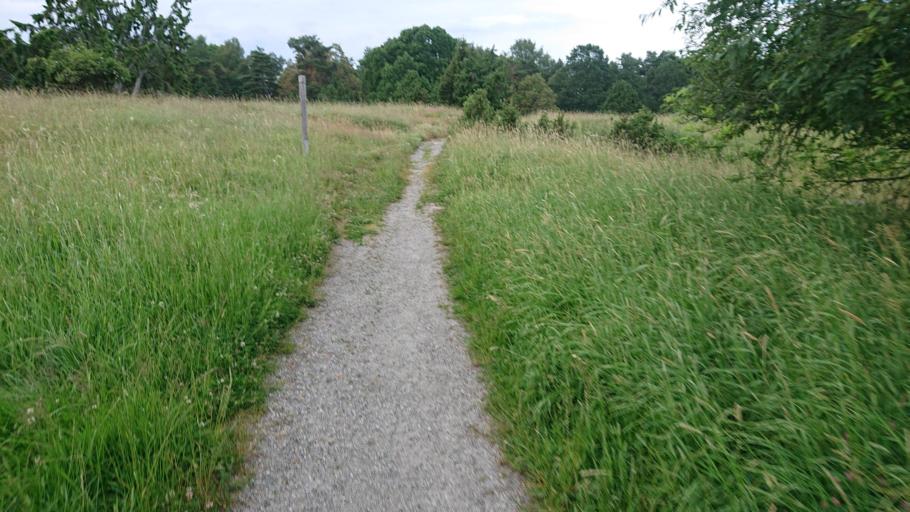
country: SE
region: Stockholm
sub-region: Osterakers Kommun
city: Akersberga
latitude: 59.4906
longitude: 18.2957
